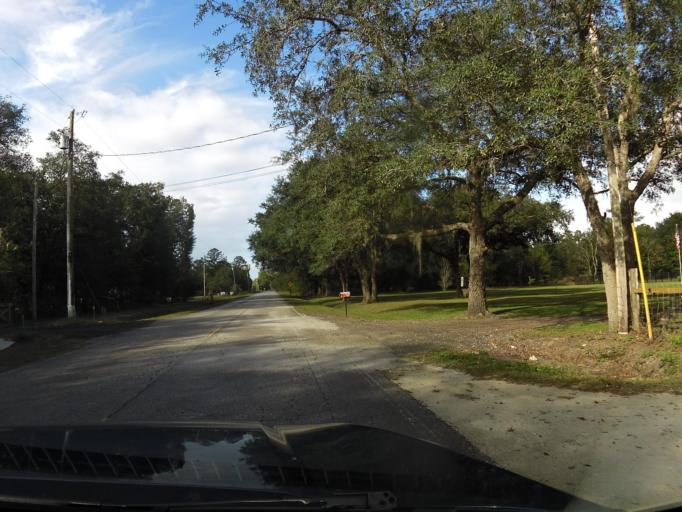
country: US
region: Florida
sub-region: Clay County
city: Asbury Lake
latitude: 29.9847
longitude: -81.8396
